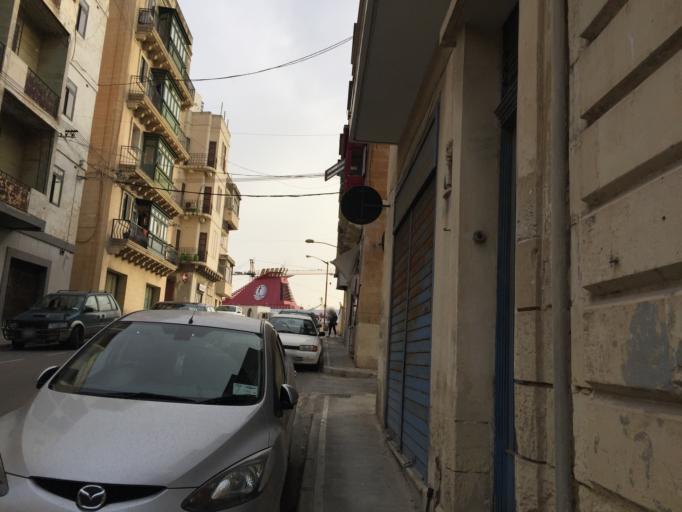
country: MT
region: L-Isla
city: Senglea
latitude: 35.8812
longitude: 14.5184
